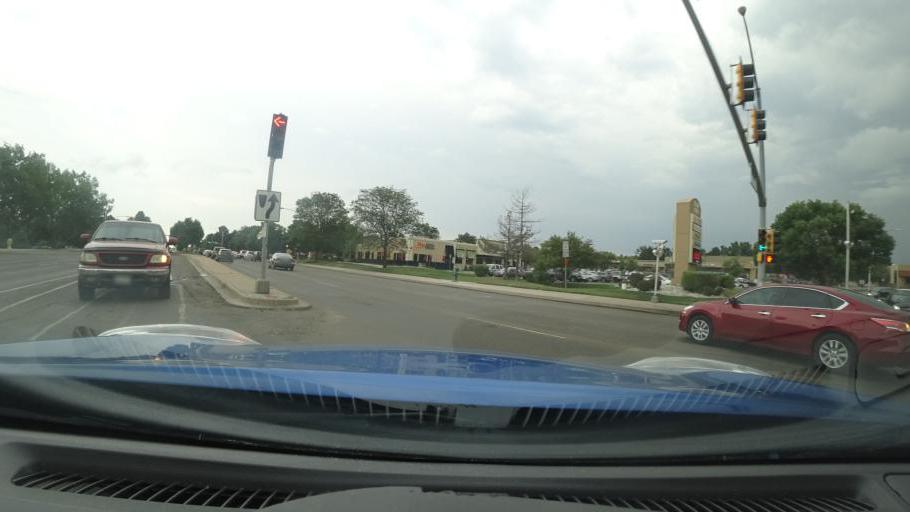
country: US
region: Colorado
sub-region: Adams County
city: Aurora
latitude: 39.6967
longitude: -104.8259
